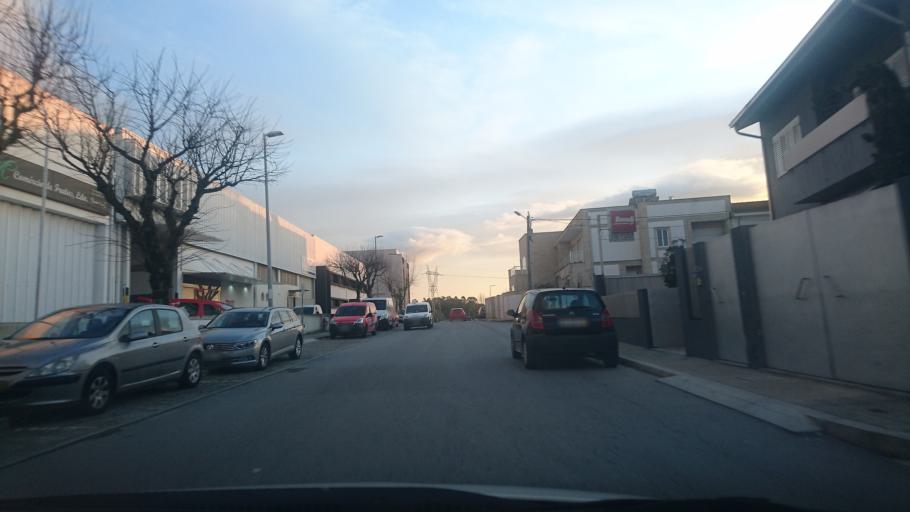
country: PT
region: Porto
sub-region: Gondomar
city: Baguim do Monte
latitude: 41.2030
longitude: -8.5450
